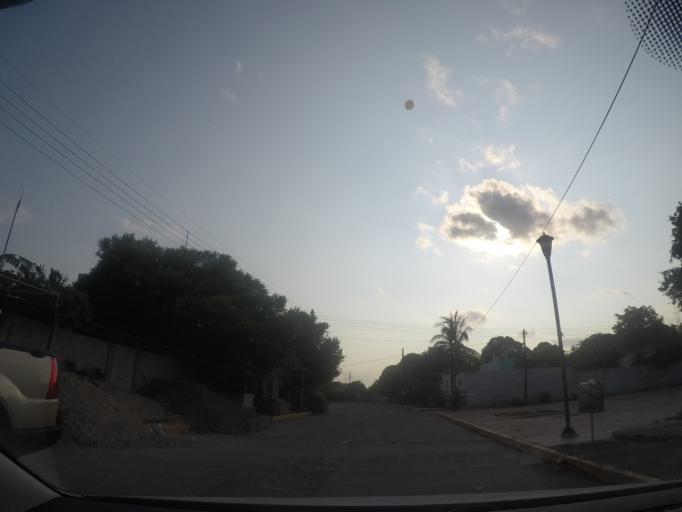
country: MX
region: Oaxaca
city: San Jeronimo Ixtepec
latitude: 16.5918
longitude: -95.1623
